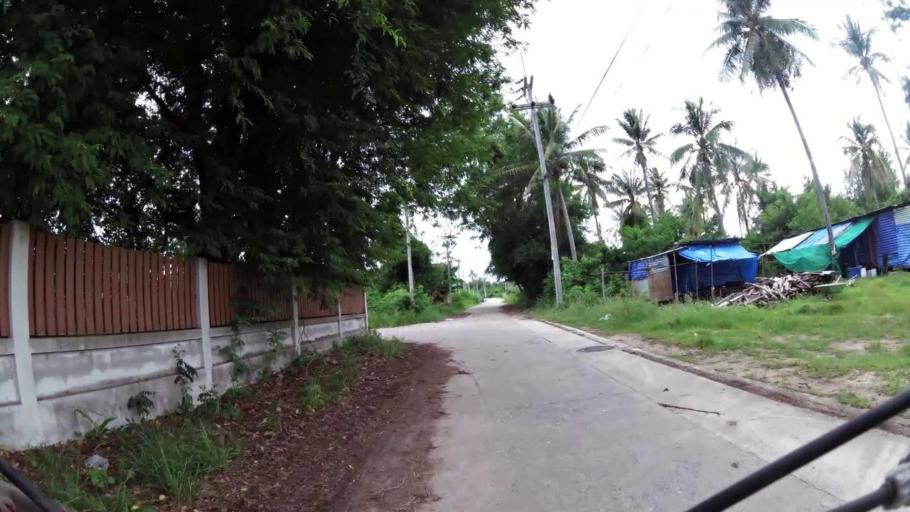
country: TH
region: Prachuap Khiri Khan
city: Prachuap Khiri Khan
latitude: 11.7367
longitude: 99.7778
